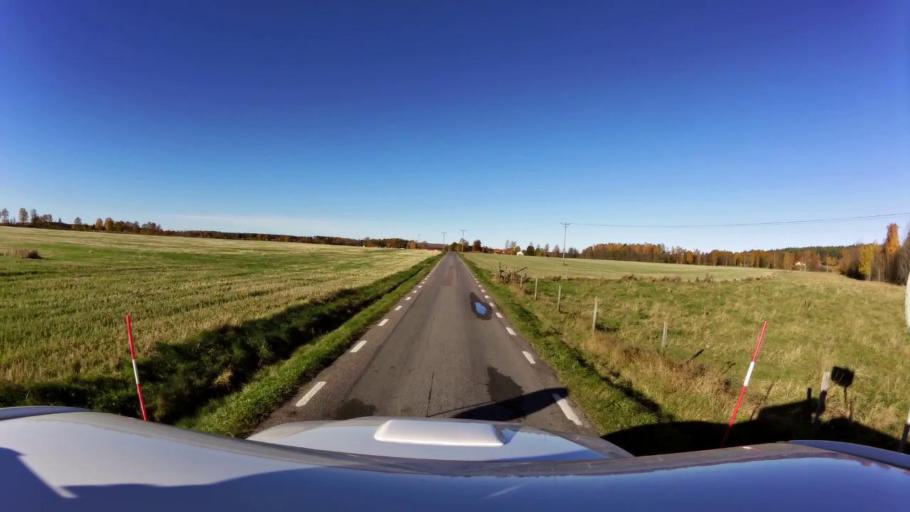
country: SE
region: OEstergoetland
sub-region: Linkopings Kommun
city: Ljungsbro
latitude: 58.5351
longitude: 15.4165
